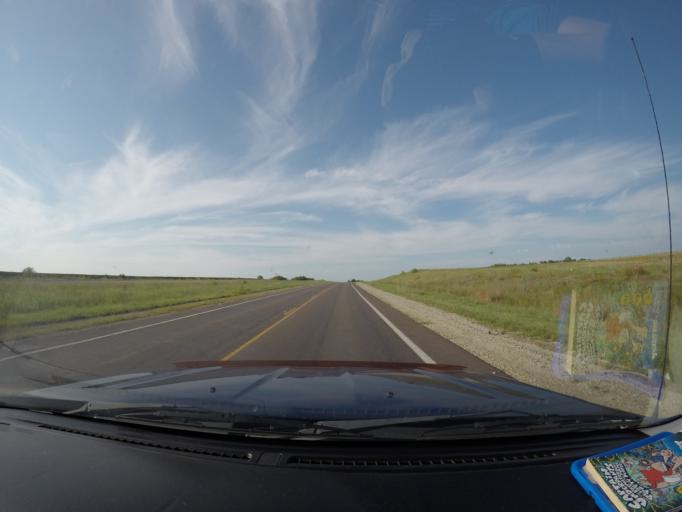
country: US
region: Kansas
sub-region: Leavenworth County
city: Leavenworth
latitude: 39.3866
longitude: -95.0578
